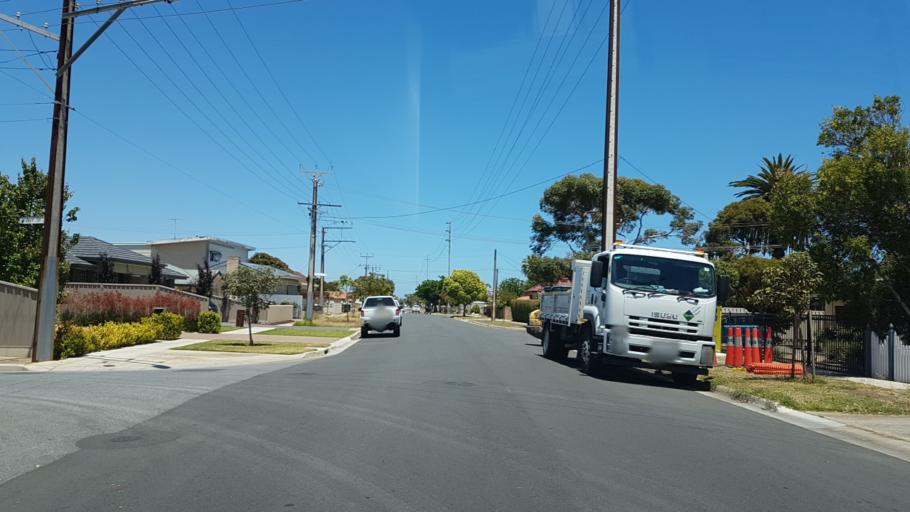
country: AU
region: South Australia
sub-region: Charles Sturt
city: West Lakes Shore
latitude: -34.8531
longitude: 138.4884
